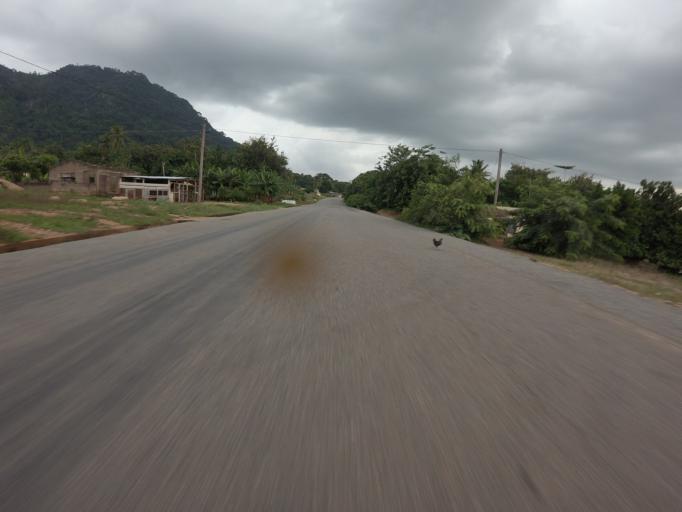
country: GH
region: Volta
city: Kpandu
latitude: 6.7974
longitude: 0.3719
